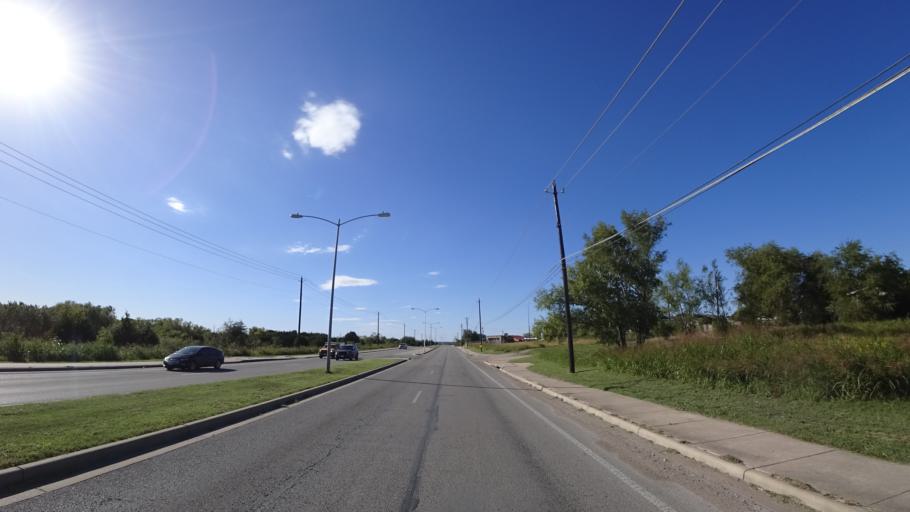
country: US
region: Texas
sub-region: Travis County
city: Hornsby Bend
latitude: 30.2920
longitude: -97.6295
